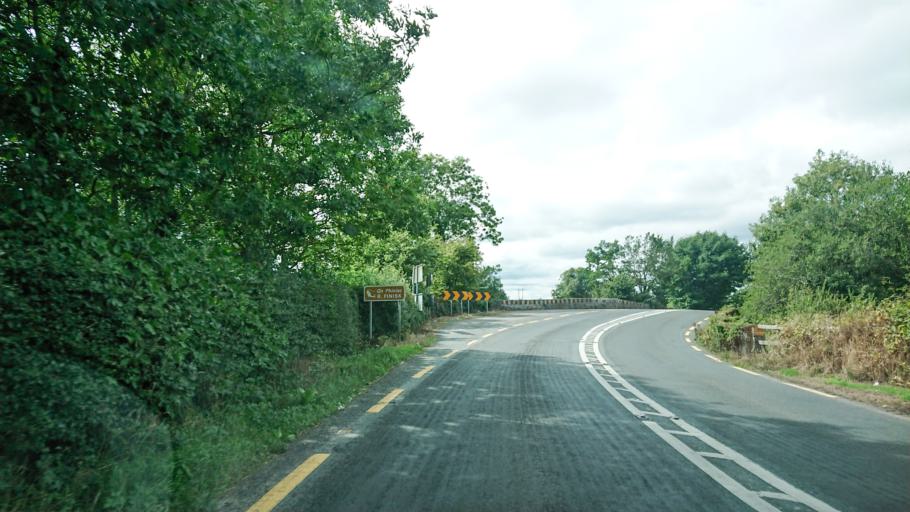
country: IE
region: Munster
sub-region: Waterford
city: Dungarvan
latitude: 52.1215
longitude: -7.7629
